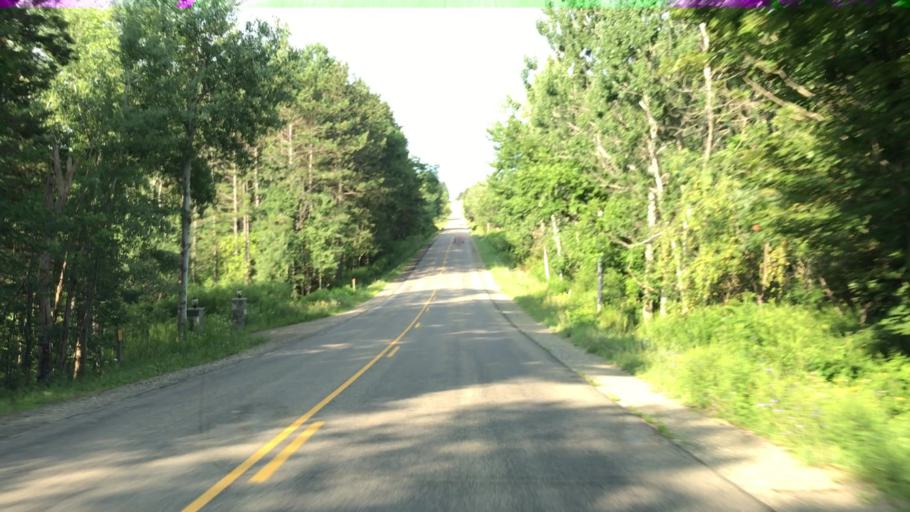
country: US
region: New York
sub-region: Chautauqua County
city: Brocton
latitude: 42.3054
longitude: -79.3857
